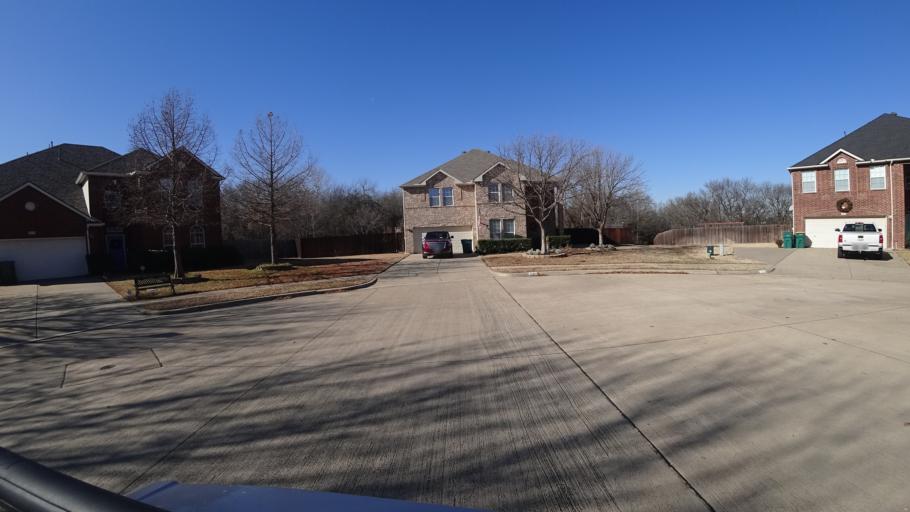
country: US
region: Texas
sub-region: Denton County
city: Lewisville
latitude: 33.0211
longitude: -97.0228
